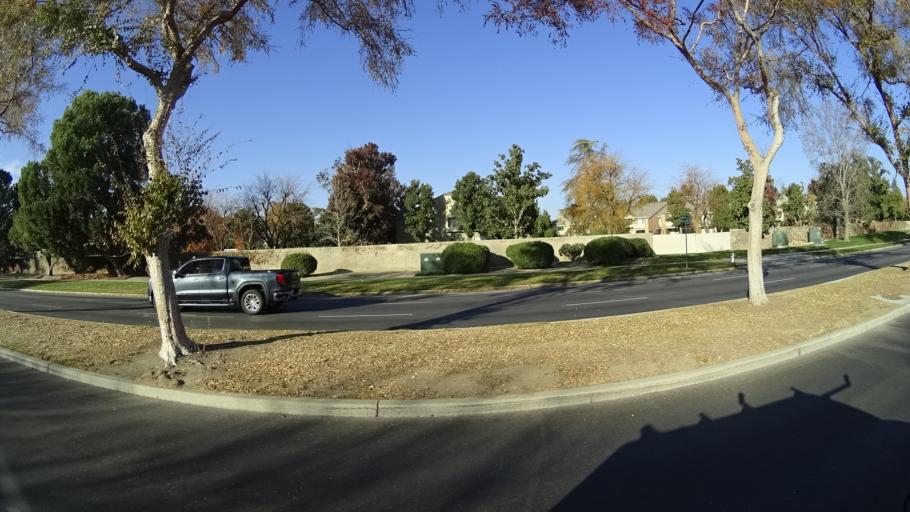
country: US
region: California
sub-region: Kern County
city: Greenacres
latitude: 35.3397
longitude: -119.0941
